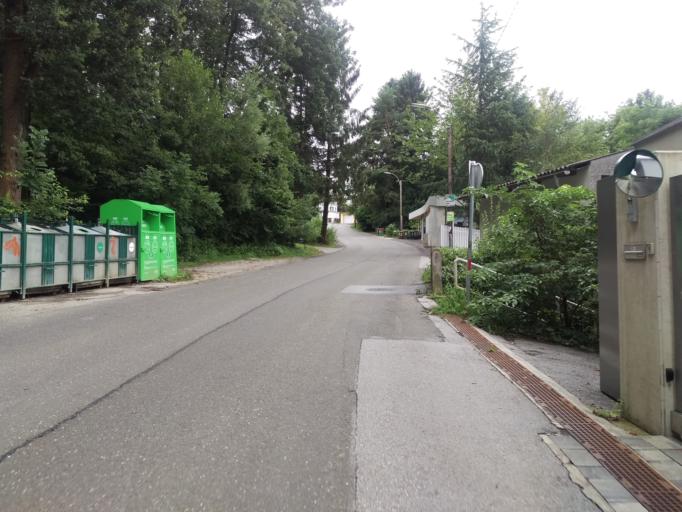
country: AT
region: Styria
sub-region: Politischer Bezirk Graz-Umgebung
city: Raaba
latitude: 47.0551
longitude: 15.4820
